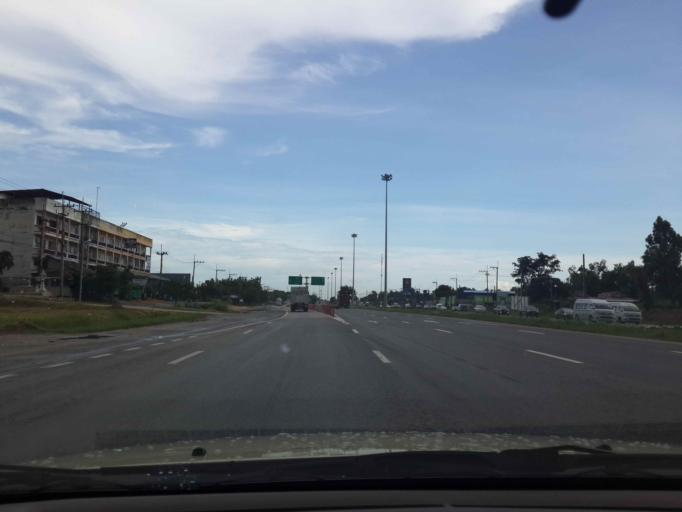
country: TH
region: Chon Buri
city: Phatthaya
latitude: 12.9575
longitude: 100.9852
